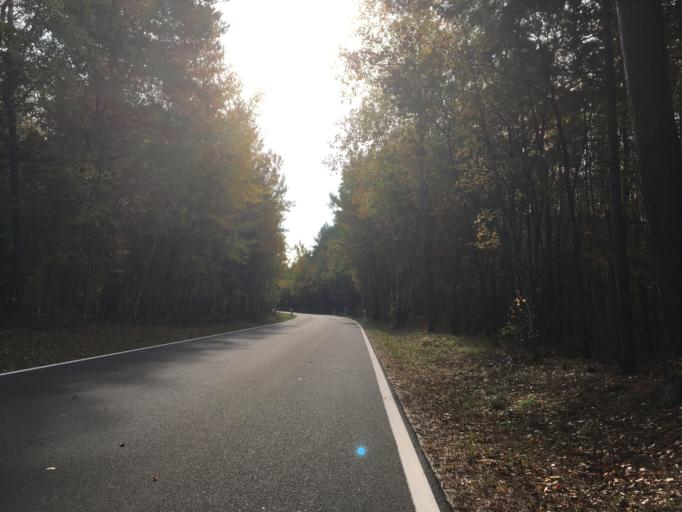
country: DE
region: Brandenburg
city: Templin
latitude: 53.0143
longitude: 13.4659
